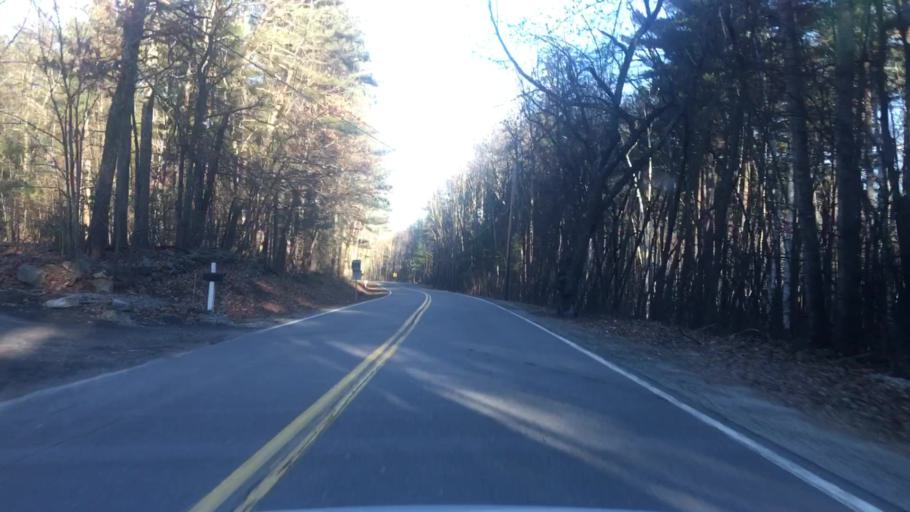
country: US
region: New Hampshire
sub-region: Rockingham County
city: Londonderry
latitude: 42.9002
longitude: -71.3681
